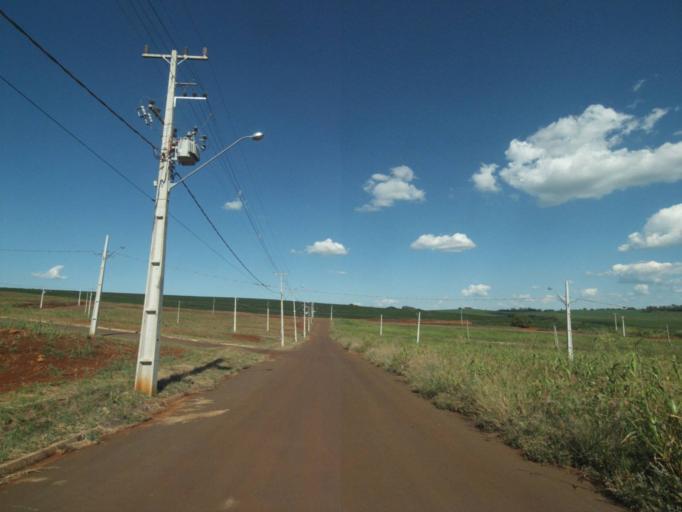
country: BR
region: Parana
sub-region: Sertanopolis
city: Sertanopolis
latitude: -23.0452
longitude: -50.8144
